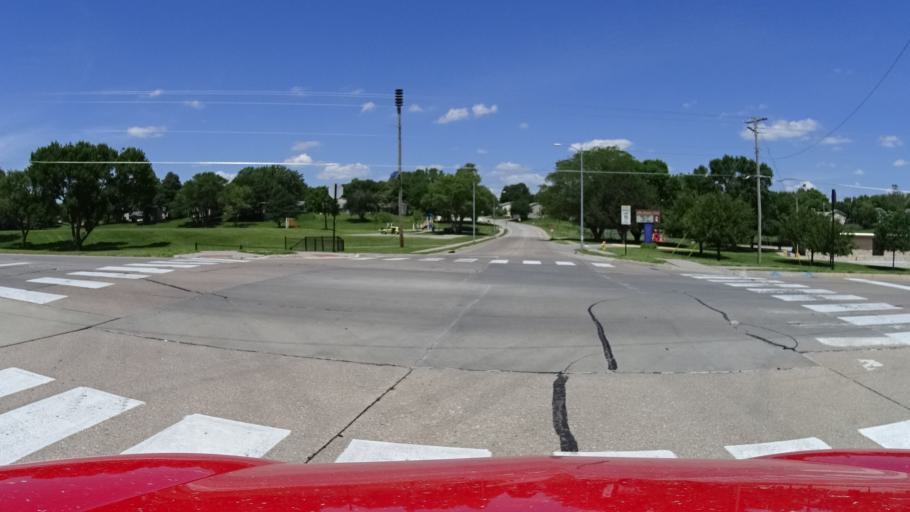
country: US
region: Nebraska
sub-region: Sarpy County
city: Offutt Air Force Base
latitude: 41.1289
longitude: -95.9518
